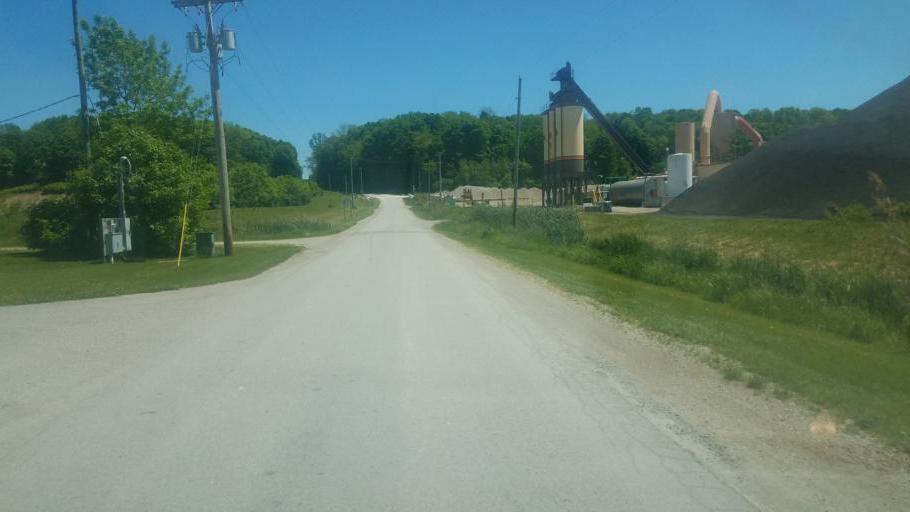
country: US
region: Ohio
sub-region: Miami County
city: Piqua
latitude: 40.2200
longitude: -84.2082
